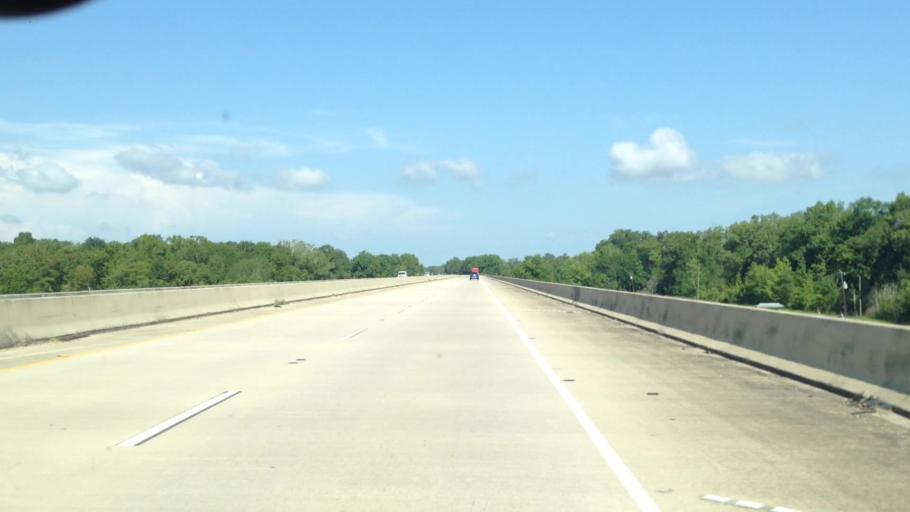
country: US
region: Louisiana
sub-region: Saint Landry Parish
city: Krotz Springs
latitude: 30.5478
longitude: -91.8264
